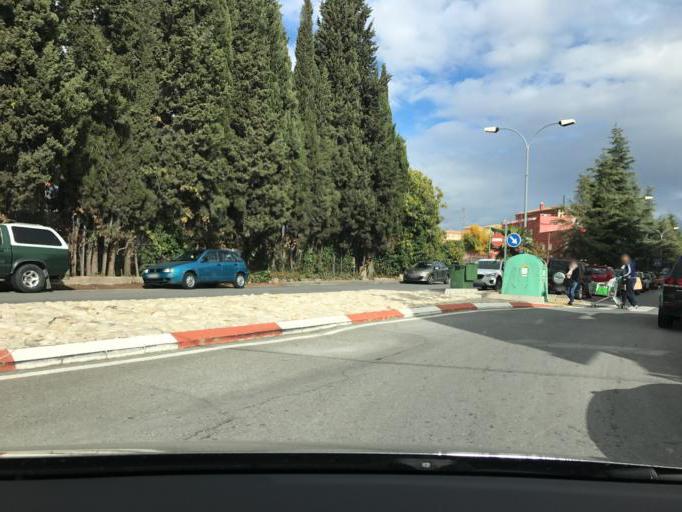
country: ES
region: Andalusia
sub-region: Provincia de Granada
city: Peligros
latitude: 37.2339
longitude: -3.6416
